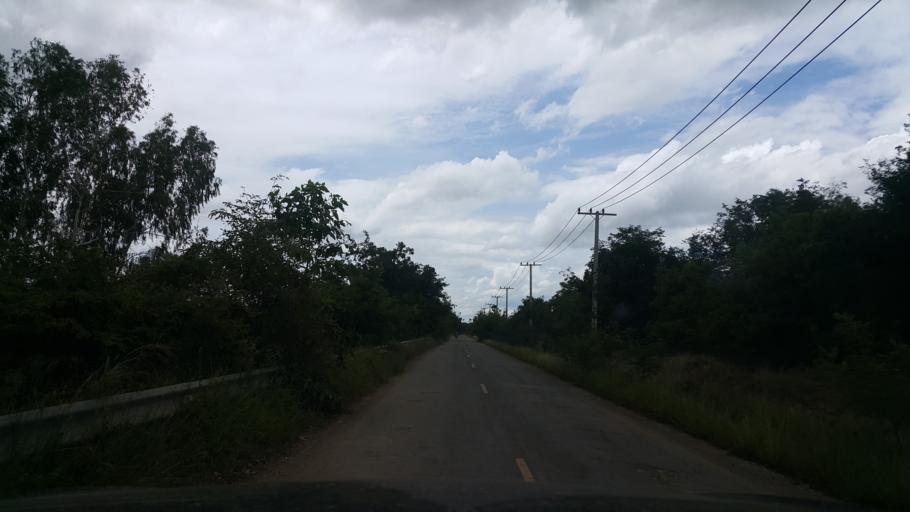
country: TH
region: Sukhothai
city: Ban Na
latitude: 17.0519
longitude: 99.7756
